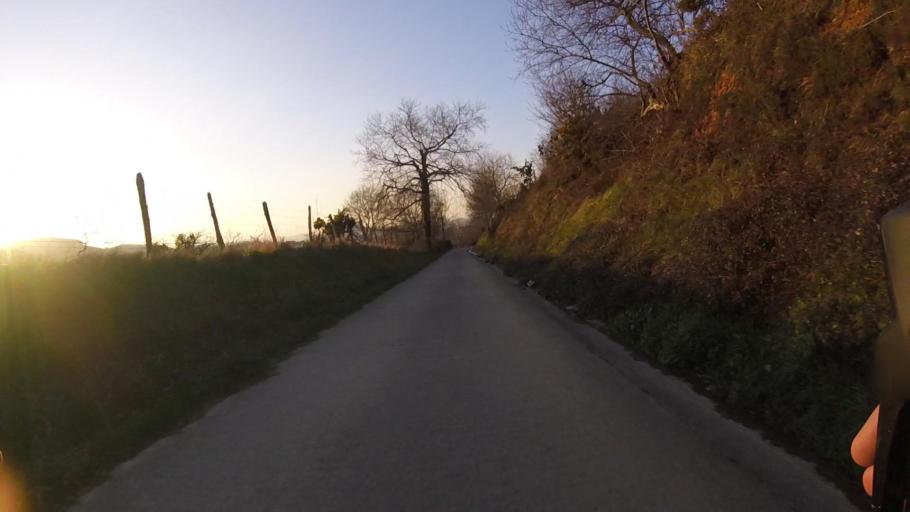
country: ES
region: Basque Country
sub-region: Provincia de Guipuzcoa
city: Errenteria
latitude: 43.2718
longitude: -1.8585
